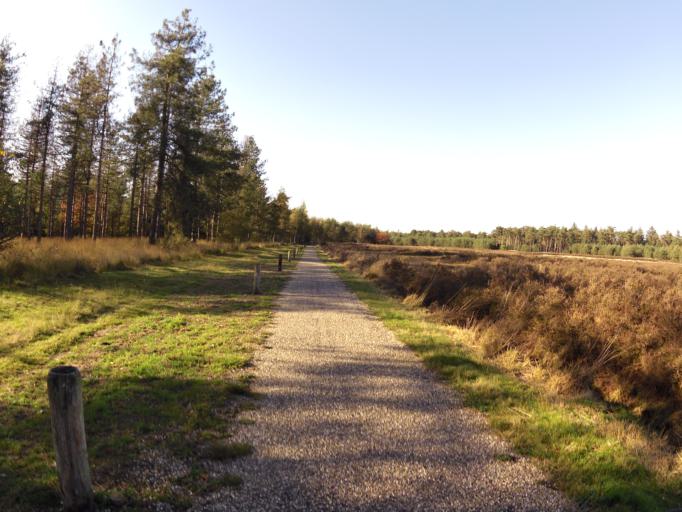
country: NL
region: North Brabant
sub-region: Gemeente Someren
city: Someren
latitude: 51.3711
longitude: 5.6537
